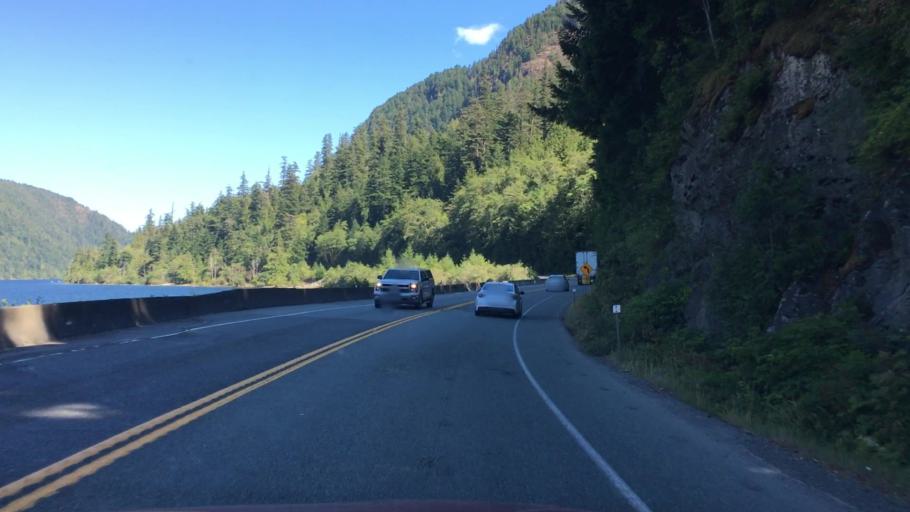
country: CA
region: British Columbia
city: Port Alberni
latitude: 49.2885
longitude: -124.6337
